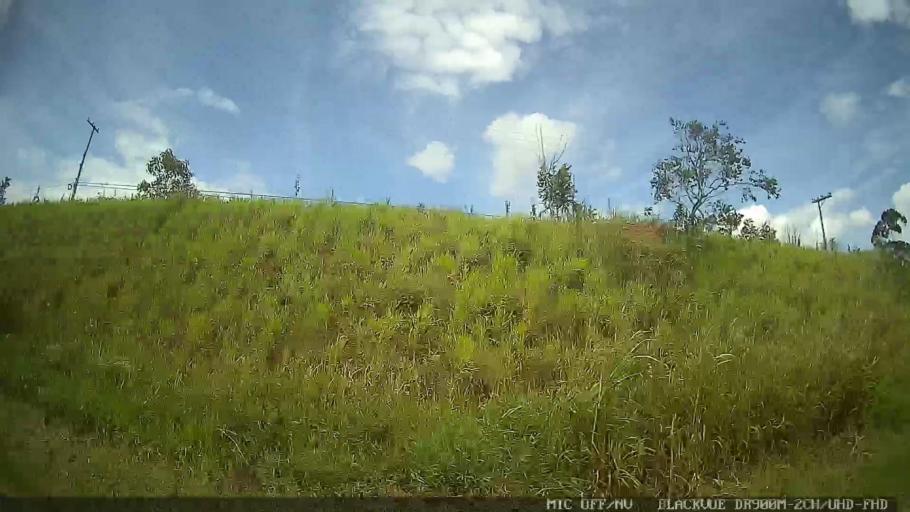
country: BR
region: Sao Paulo
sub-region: Suzano
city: Suzano
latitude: -23.6278
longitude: -46.2571
